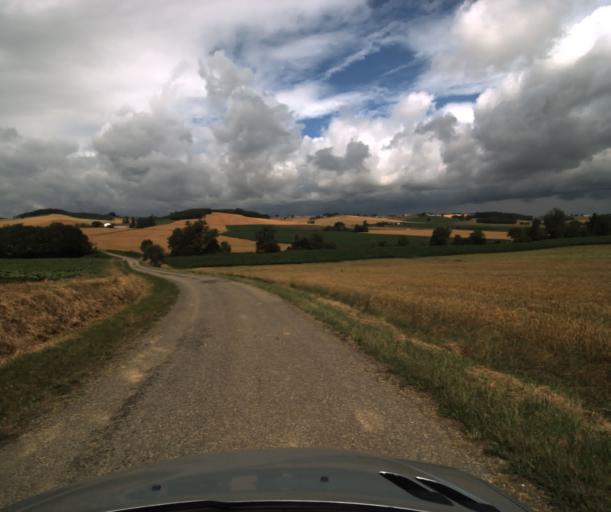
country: FR
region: Midi-Pyrenees
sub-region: Departement du Tarn-et-Garonne
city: Lavit
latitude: 43.9547
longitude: 0.9091
